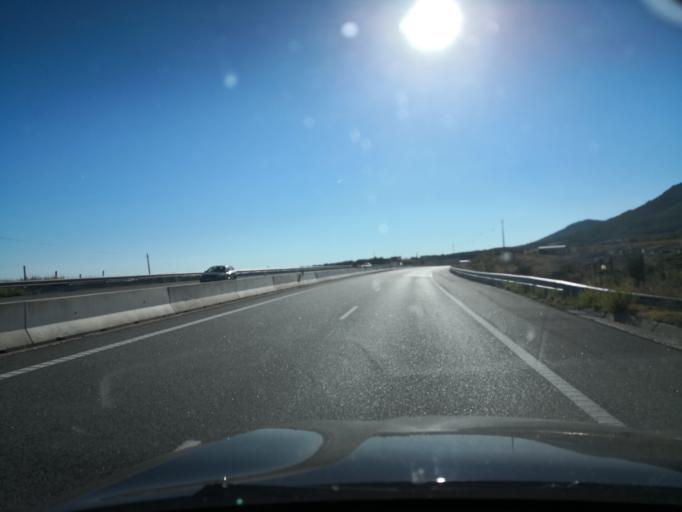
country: PT
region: Braganca
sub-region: Mirandela
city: Mirandela
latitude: 41.4649
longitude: -7.2460
